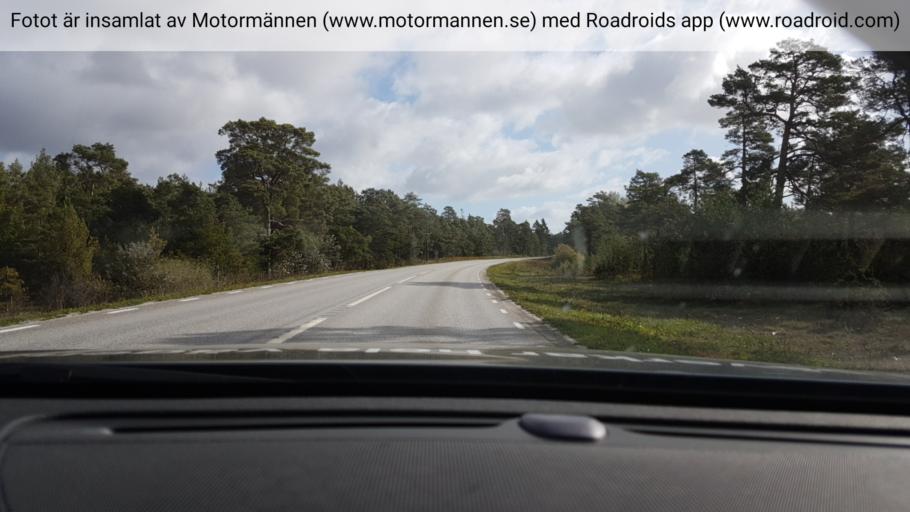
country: SE
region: Gotland
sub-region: Gotland
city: Slite
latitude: 57.8398
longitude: 18.9429
